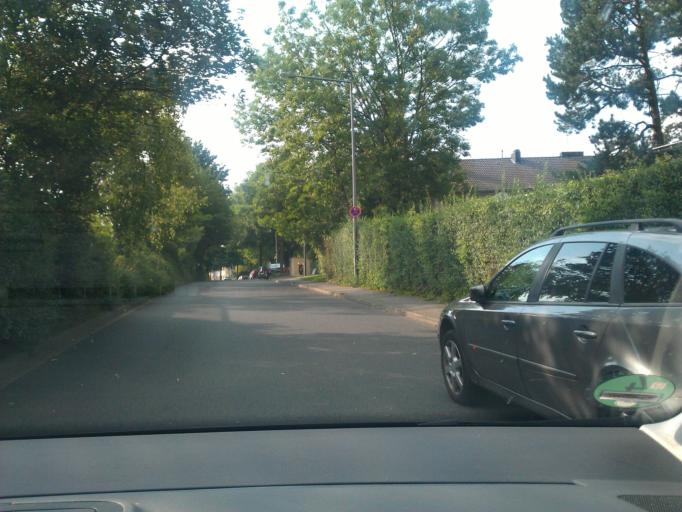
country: DE
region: North Rhine-Westphalia
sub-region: Regierungsbezirk Koln
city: Aachen
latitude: 50.7831
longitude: 6.0603
